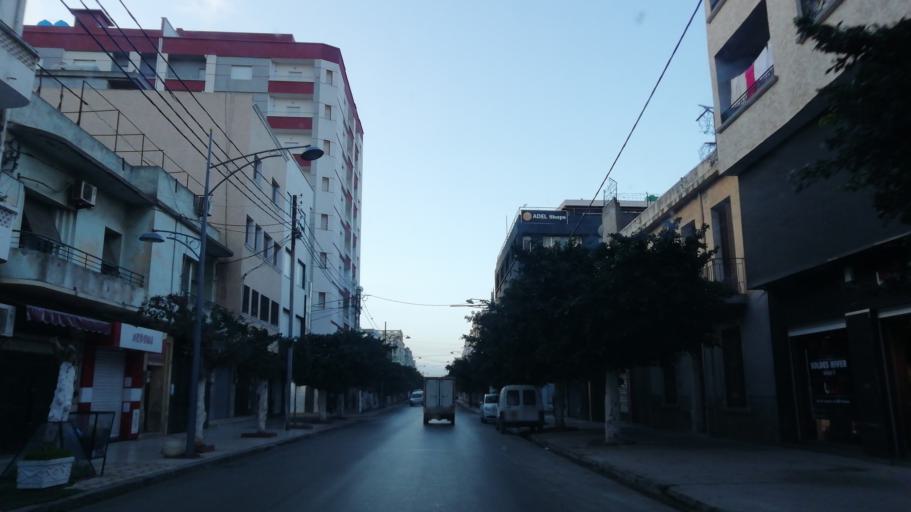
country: DZ
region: Oran
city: Oran
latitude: 35.6828
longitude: -0.6556
